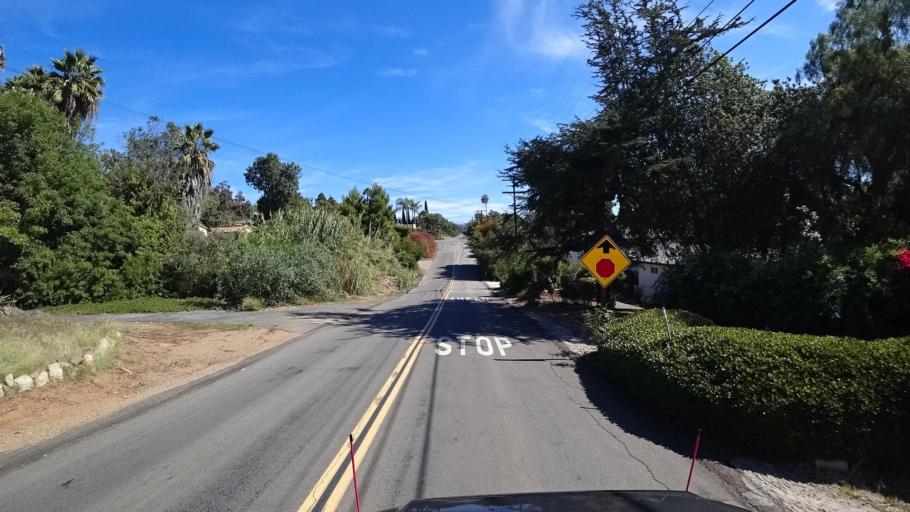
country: US
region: California
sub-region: San Diego County
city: Casa de Oro-Mount Helix
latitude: 32.7555
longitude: -116.9692
